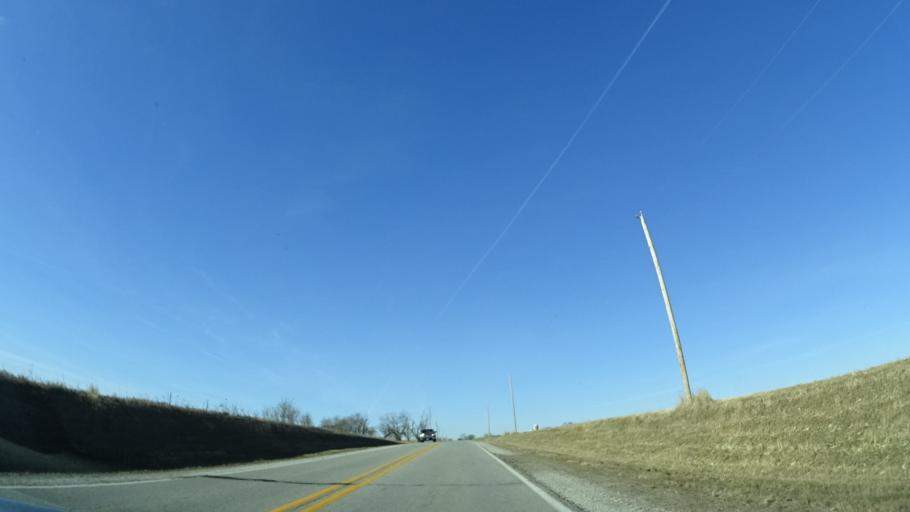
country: US
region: Nebraska
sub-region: Sarpy County
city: Papillion
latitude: 41.0891
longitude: -96.0636
